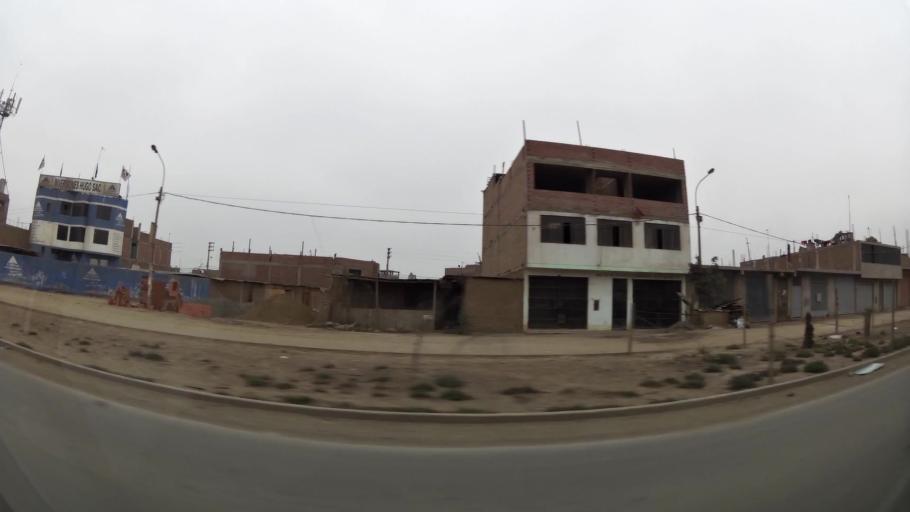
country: PE
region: Lima
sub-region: Lima
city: Urb. Santo Domingo
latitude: -11.8729
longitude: -77.0230
